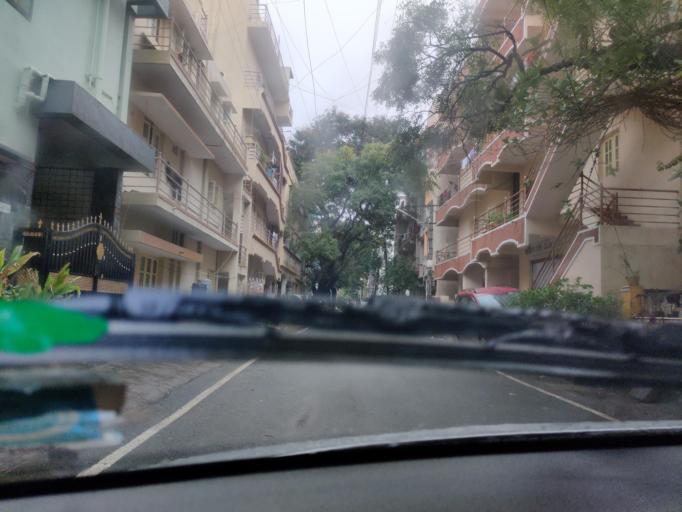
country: IN
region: Karnataka
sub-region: Bangalore Urban
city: Bangalore
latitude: 13.0224
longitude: 77.6325
